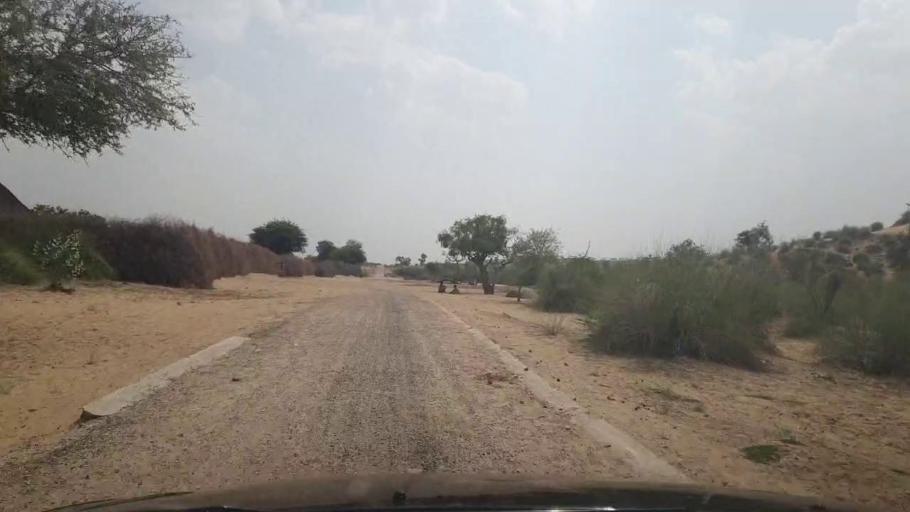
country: PK
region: Sindh
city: Islamkot
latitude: 25.0115
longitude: 70.5269
